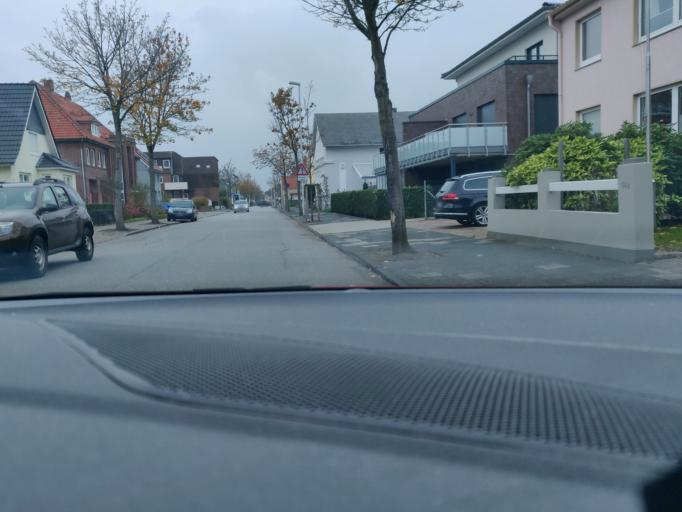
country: DE
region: Lower Saxony
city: Cuxhaven
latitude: 53.8834
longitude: 8.6700
